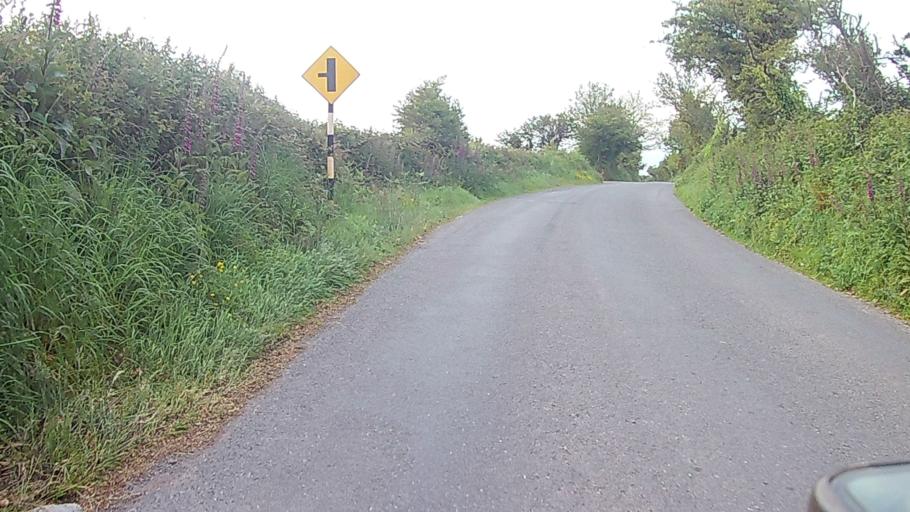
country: IE
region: Munster
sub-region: County Cork
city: Watergrasshill
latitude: 51.9697
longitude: -8.4118
